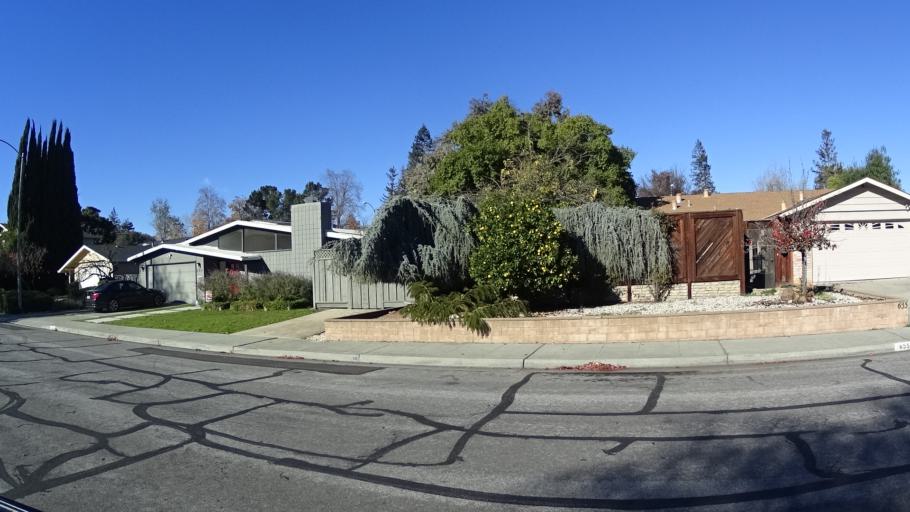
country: US
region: California
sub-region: Santa Clara County
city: Sunnyvale
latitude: 37.3516
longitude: -122.0239
